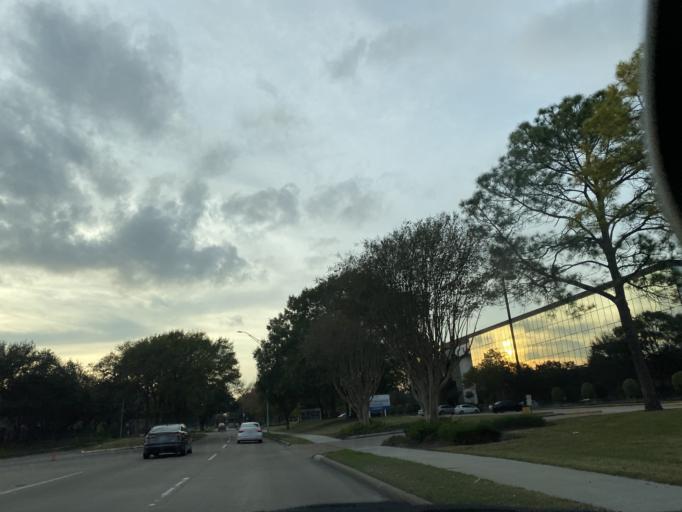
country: US
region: Texas
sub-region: Harris County
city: Bunker Hill Village
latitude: 29.7278
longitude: -95.5634
